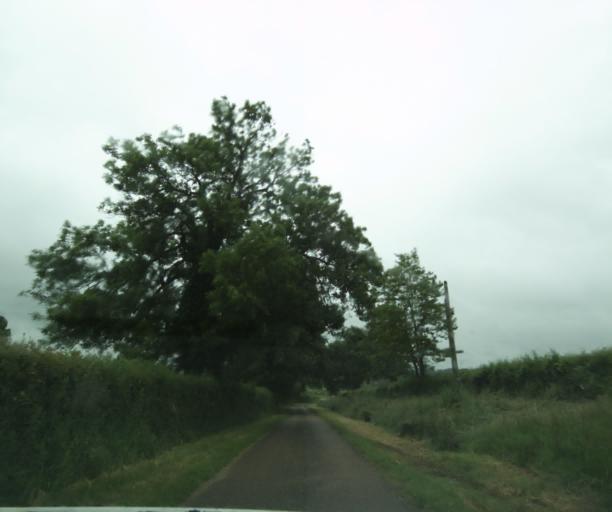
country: FR
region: Bourgogne
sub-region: Departement de Saone-et-Loire
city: Palinges
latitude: 46.4925
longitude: 4.1947
